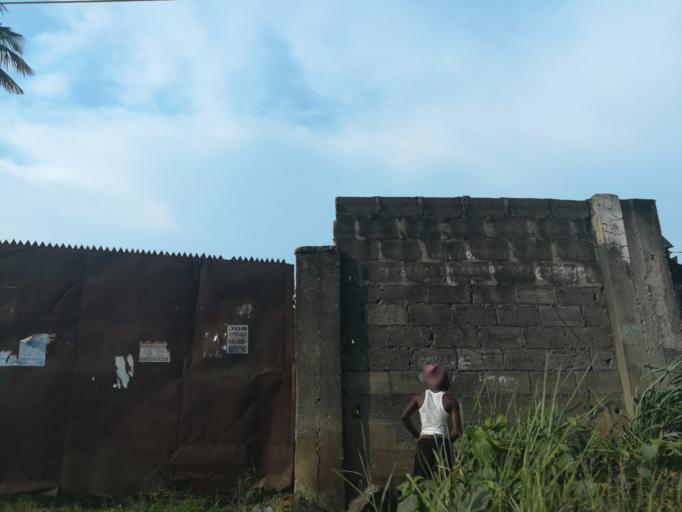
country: NG
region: Lagos
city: Ojota
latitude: 6.5964
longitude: 3.3976
